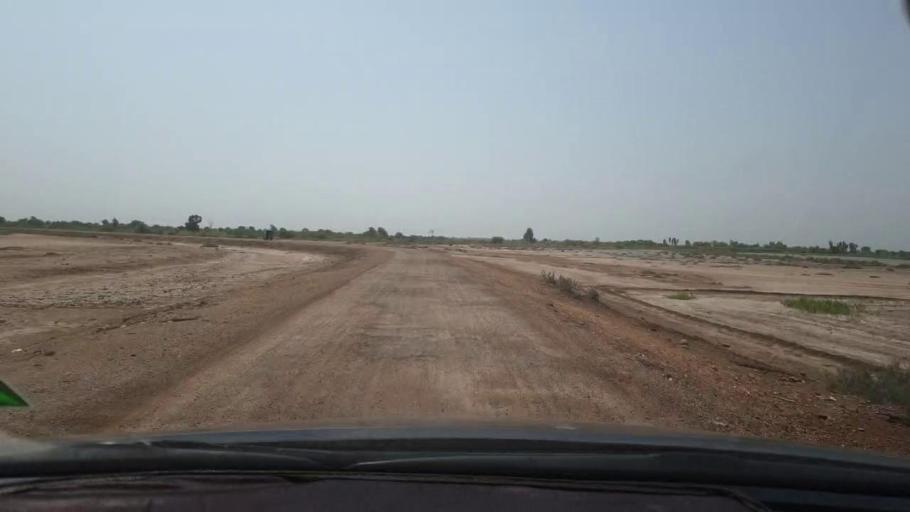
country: PK
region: Sindh
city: Tando Bago
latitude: 24.7954
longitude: 69.1676
